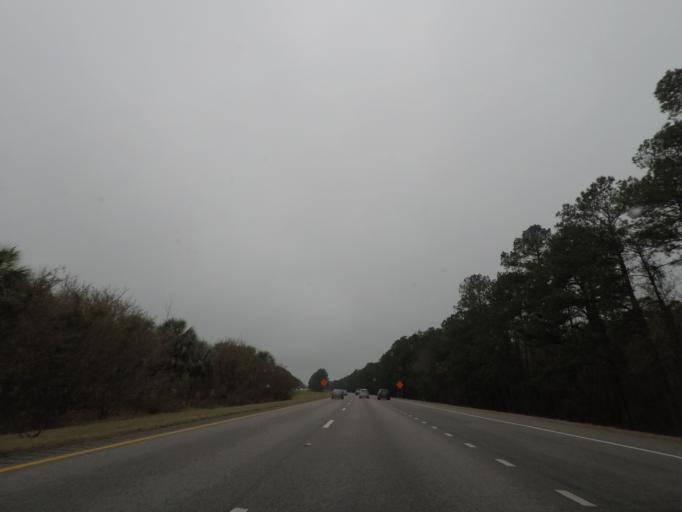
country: US
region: South Carolina
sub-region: Sumter County
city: East Sumter
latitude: 33.8974
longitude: -80.0956
